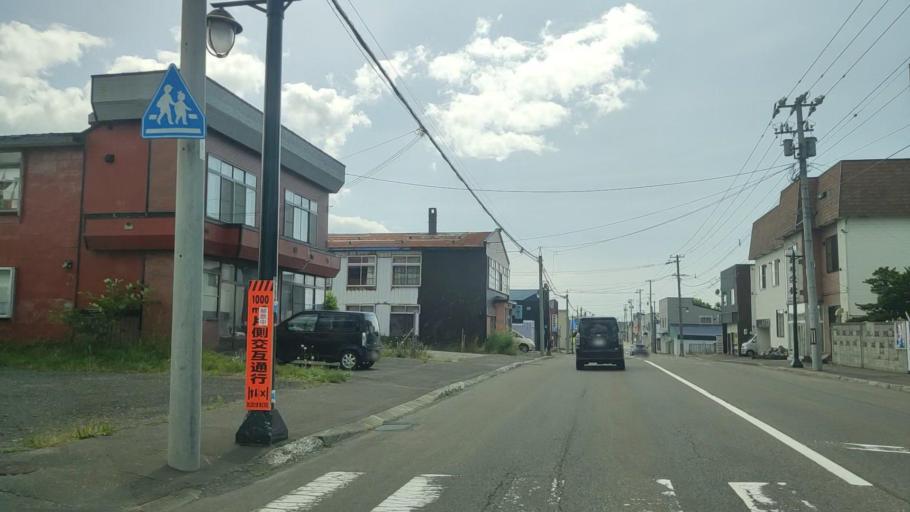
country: JP
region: Hokkaido
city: Makubetsu
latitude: 44.7239
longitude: 141.7978
